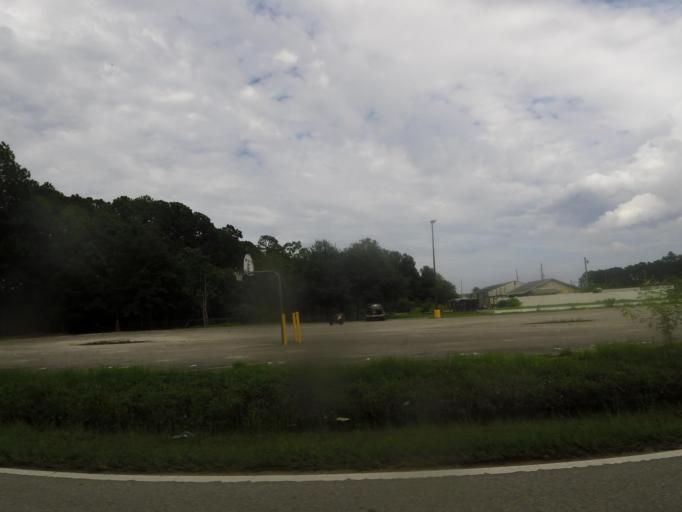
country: US
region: Florida
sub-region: Duval County
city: Jacksonville
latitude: 30.3076
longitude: -81.5313
